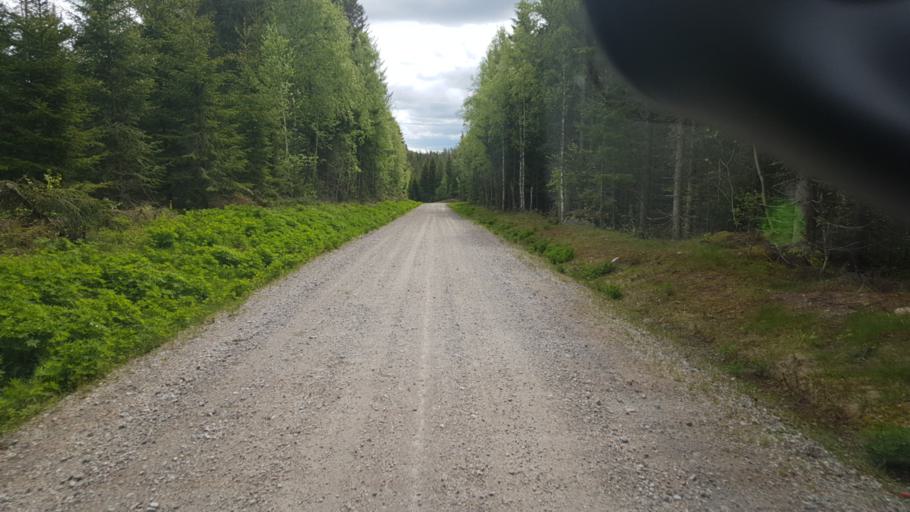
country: SE
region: Vaermland
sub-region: Arvika Kommun
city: Arvika
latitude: 59.8365
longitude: 12.8083
